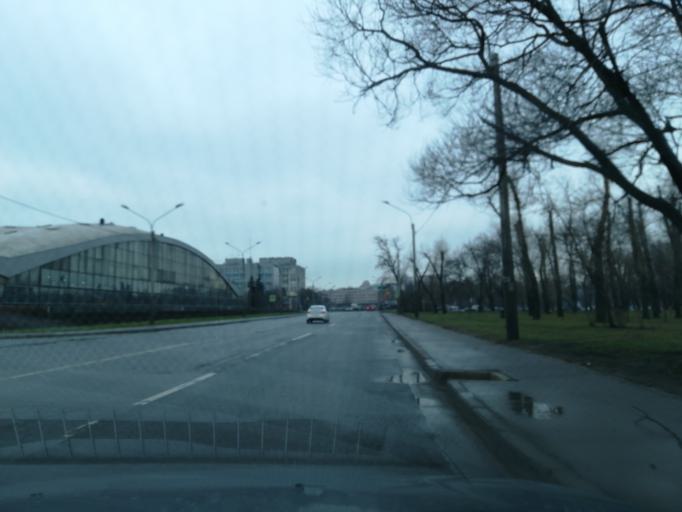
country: RU
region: St.-Petersburg
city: Avtovo
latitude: 59.8611
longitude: 30.2609
